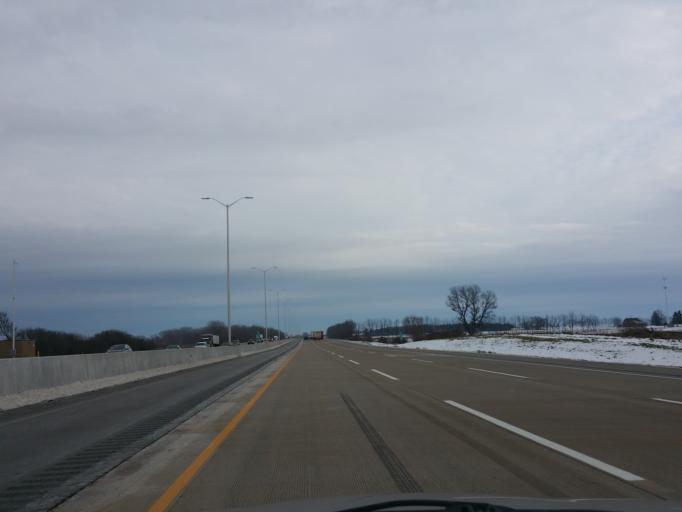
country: US
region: Illinois
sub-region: McHenry County
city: Marengo
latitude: 42.2028
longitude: -88.6929
